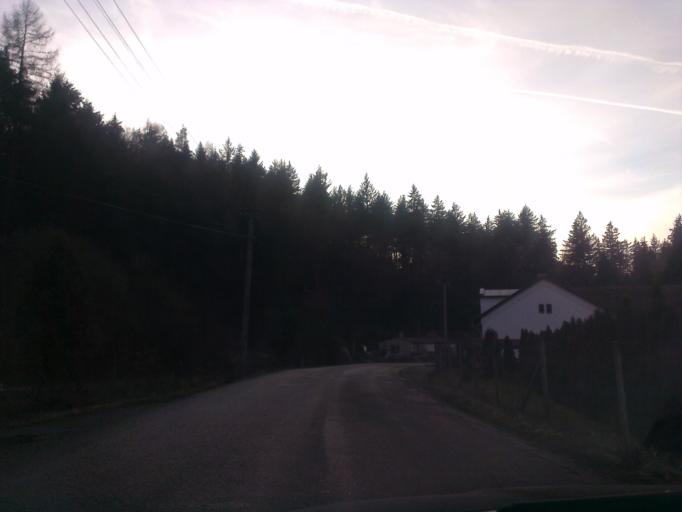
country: CZ
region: South Moravian
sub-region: Okres Blansko
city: Jedovnice
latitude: 49.2922
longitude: 16.7563
